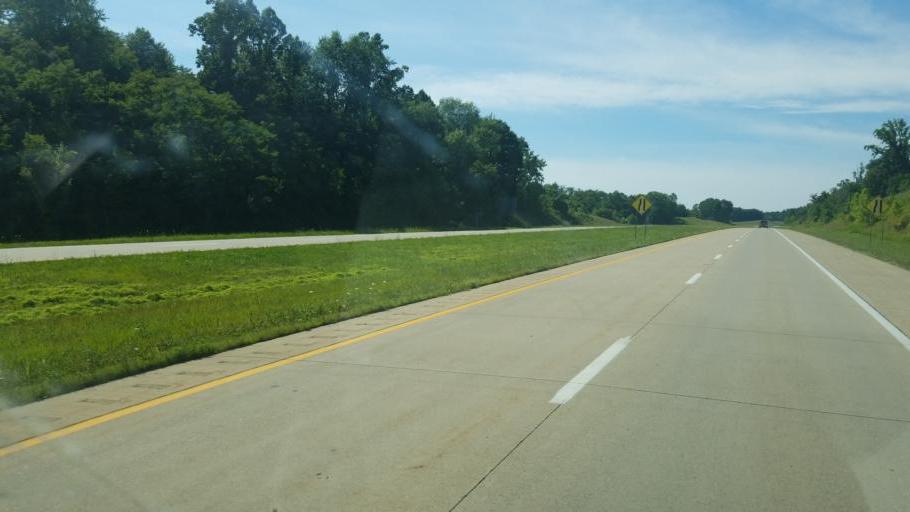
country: US
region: Ohio
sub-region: Meigs County
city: Pomeroy
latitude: 39.1474
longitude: -82.0262
